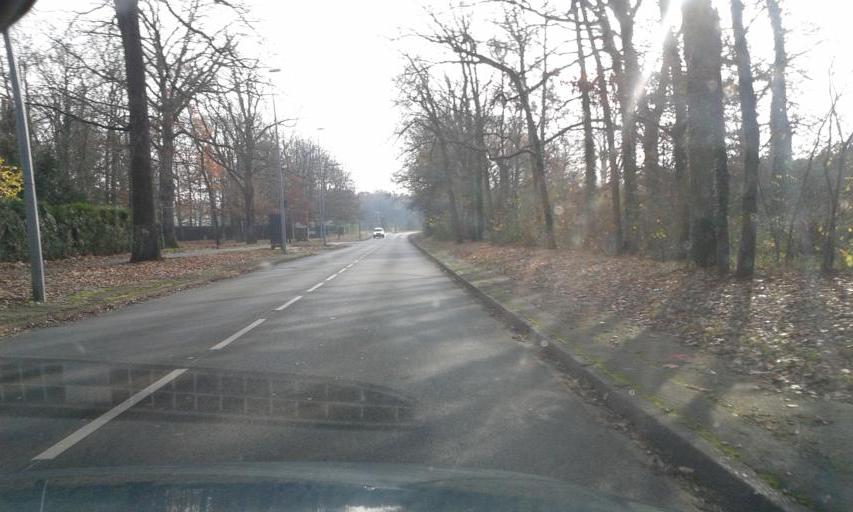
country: FR
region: Centre
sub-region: Departement du Loiret
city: Saint-Cyr-en-Val
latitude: 47.8161
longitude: 1.9278
